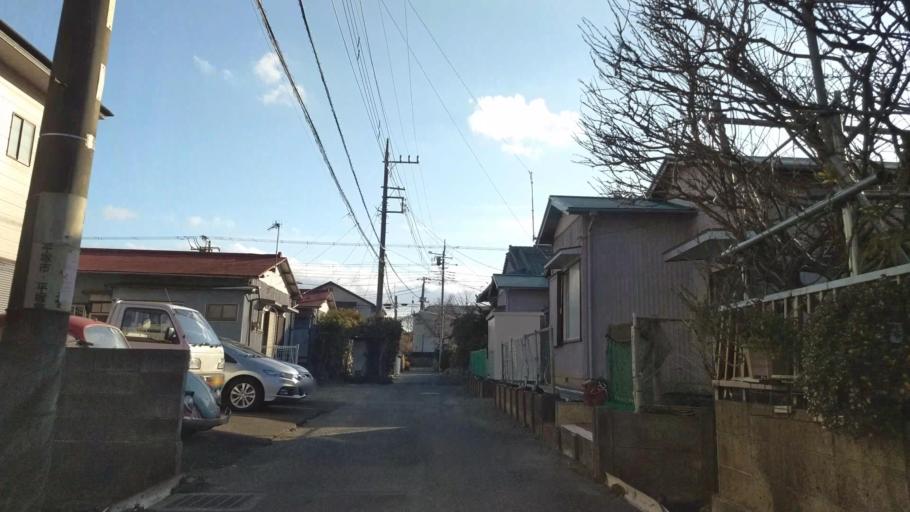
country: JP
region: Kanagawa
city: Isehara
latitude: 35.3576
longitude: 139.3056
